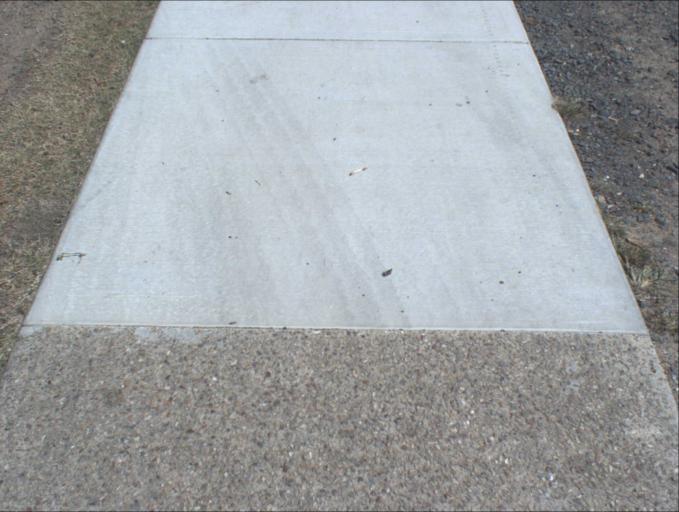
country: AU
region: Queensland
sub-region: Logan
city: Windaroo
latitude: -27.7362
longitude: 153.1938
